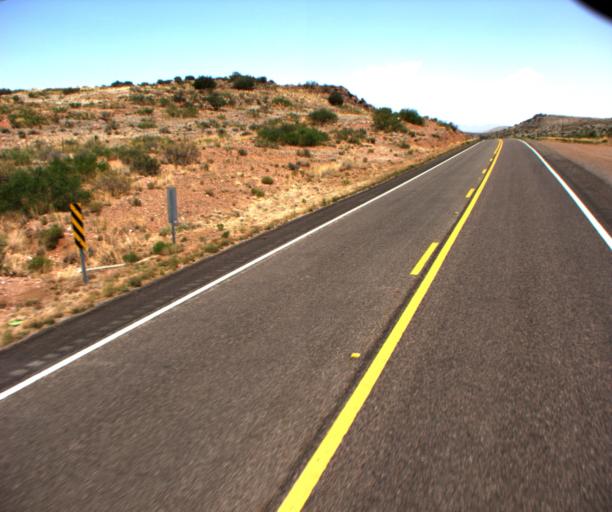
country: US
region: Arizona
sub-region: Greenlee County
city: Clifton
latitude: 32.7743
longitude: -109.2827
